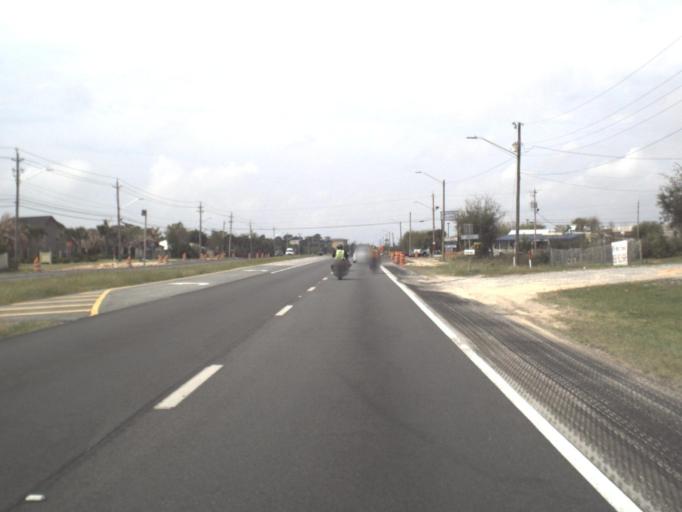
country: US
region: Florida
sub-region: Santa Rosa County
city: Navarre
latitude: 30.4066
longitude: -86.8484
